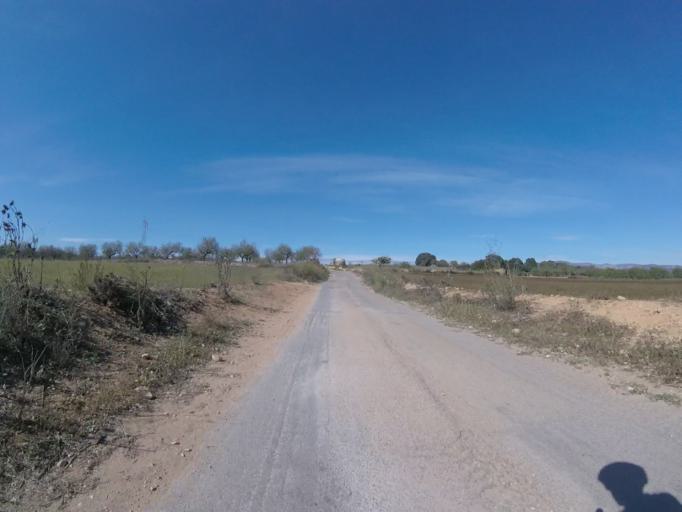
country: ES
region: Valencia
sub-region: Provincia de Castello
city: Benlloch
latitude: 40.2093
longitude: 0.0426
